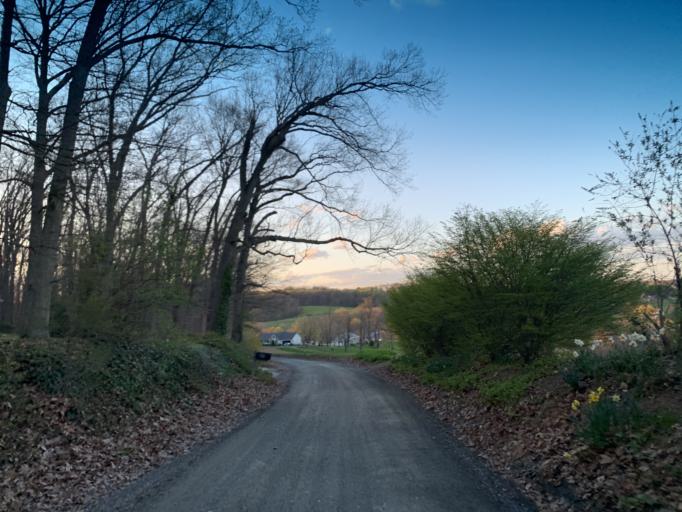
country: US
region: Maryland
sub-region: Harford County
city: Bel Air North
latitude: 39.6153
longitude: -76.3587
